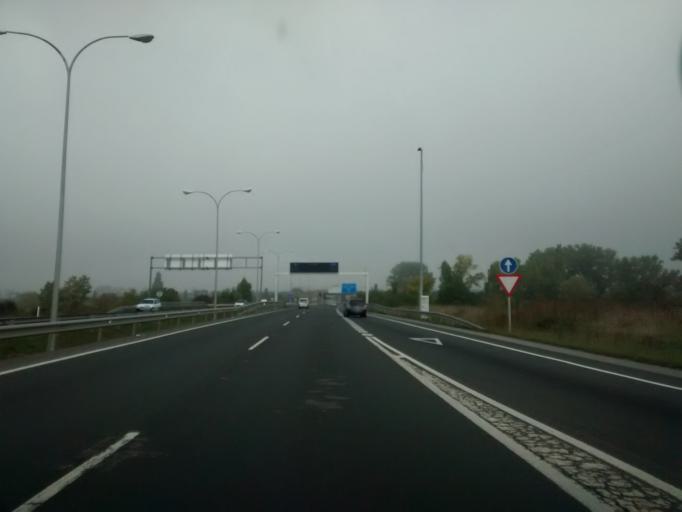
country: ES
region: Basque Country
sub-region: Provincia de Alava
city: Gasteiz / Vitoria
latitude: 42.8749
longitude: -2.6923
